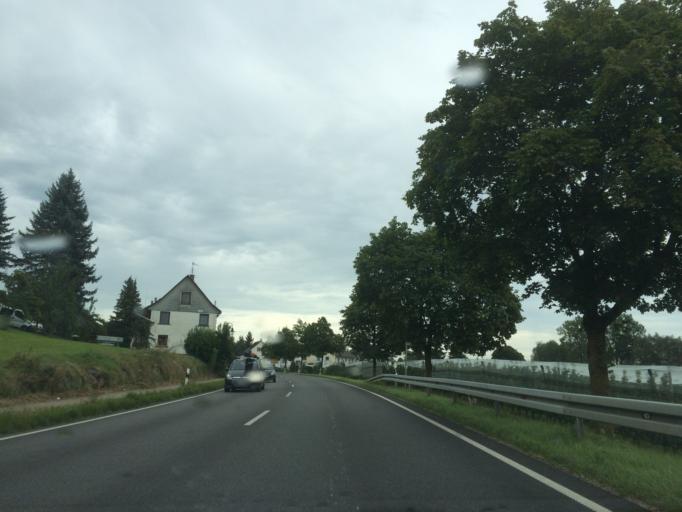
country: DE
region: Baden-Wuerttemberg
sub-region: Tuebingen Region
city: Markdorf
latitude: 47.7162
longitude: 9.4244
